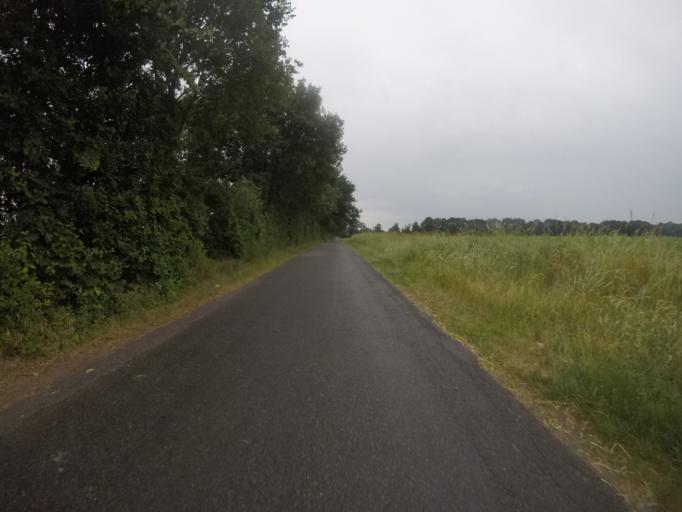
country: DE
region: North Rhine-Westphalia
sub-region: Regierungsbezirk Dusseldorf
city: Bocholt
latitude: 51.8389
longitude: 6.5654
